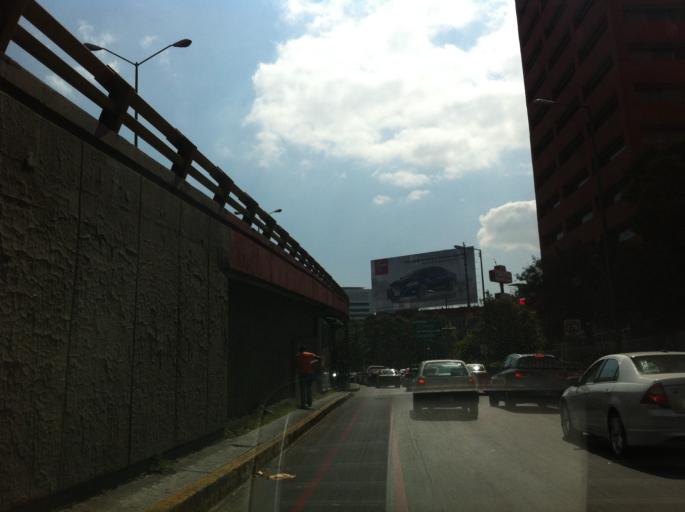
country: MX
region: Mexico City
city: Cuauhtemoc
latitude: 19.4369
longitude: -99.1707
